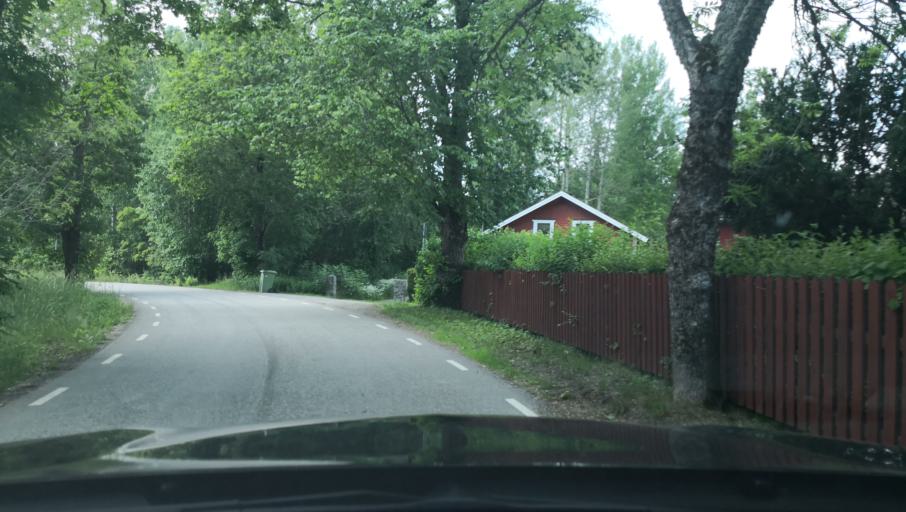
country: SE
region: Vaestmanland
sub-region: Norbergs Kommun
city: Norberg
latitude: 59.9813
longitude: 15.9576
